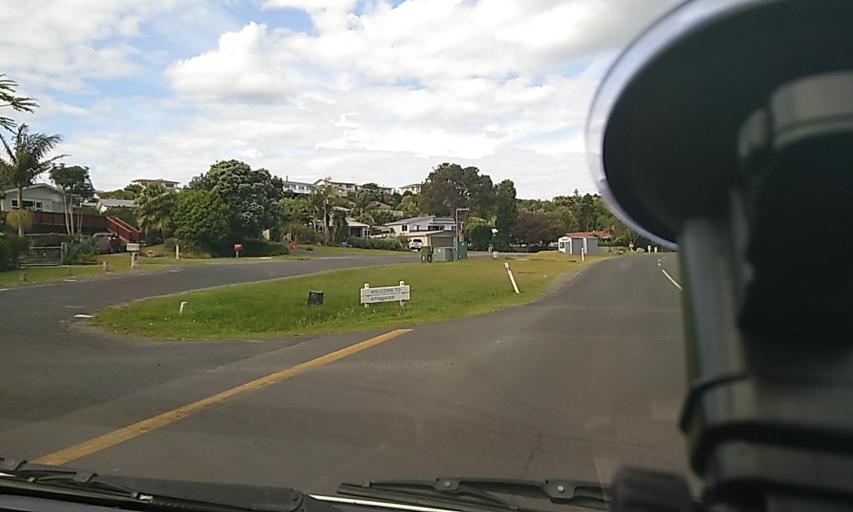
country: NZ
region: Bay of Plenty
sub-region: Western Bay of Plenty District
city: Waihi Beach
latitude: -37.4466
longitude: 175.9571
